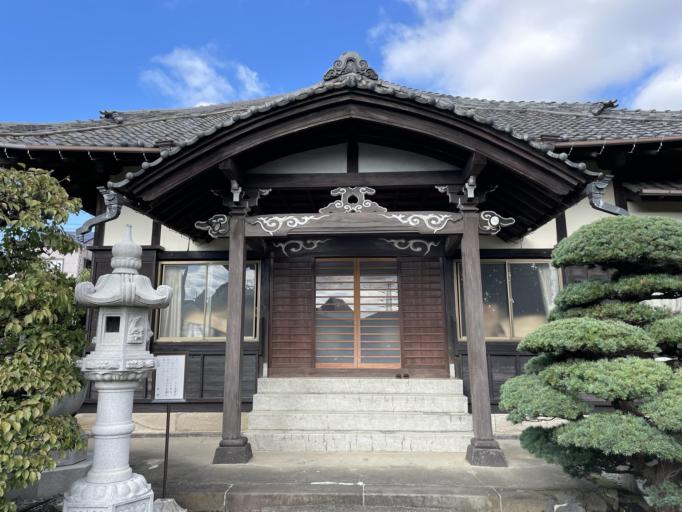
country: JP
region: Saitama
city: Soka
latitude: 35.7893
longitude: 139.7663
